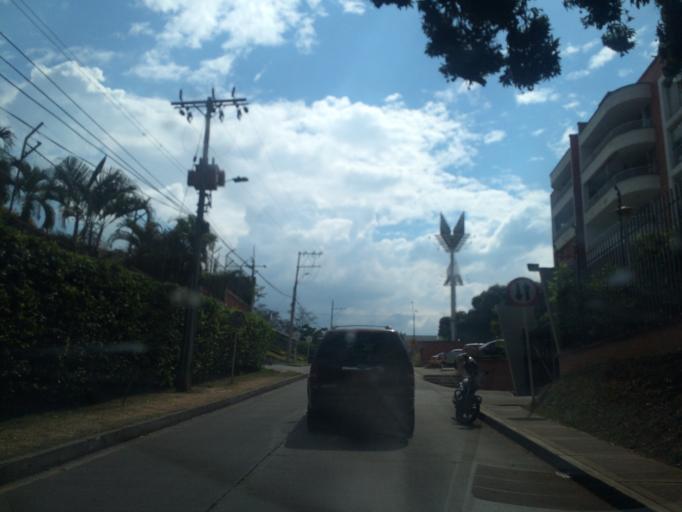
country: CO
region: Valle del Cauca
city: Jamundi
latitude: 3.3471
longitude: -76.5294
